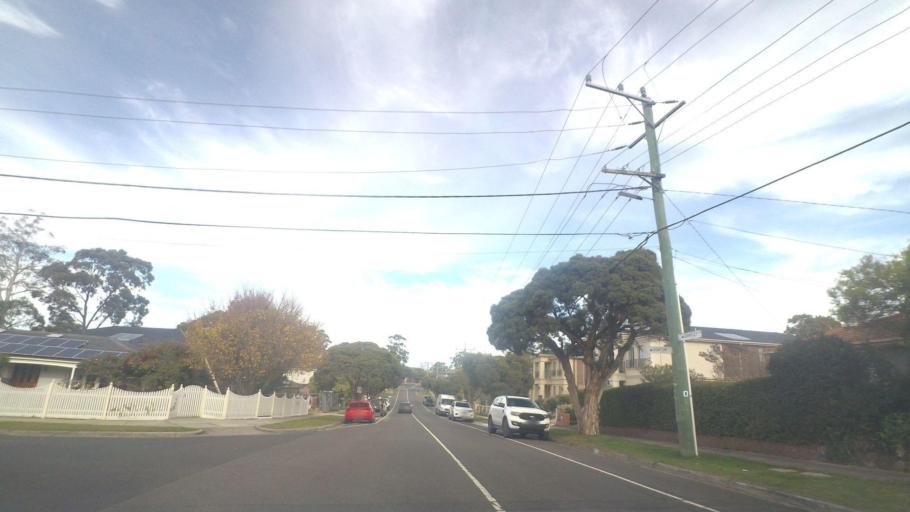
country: AU
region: Victoria
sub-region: Whitehorse
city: Vermont South
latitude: -37.8659
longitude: 145.1720
